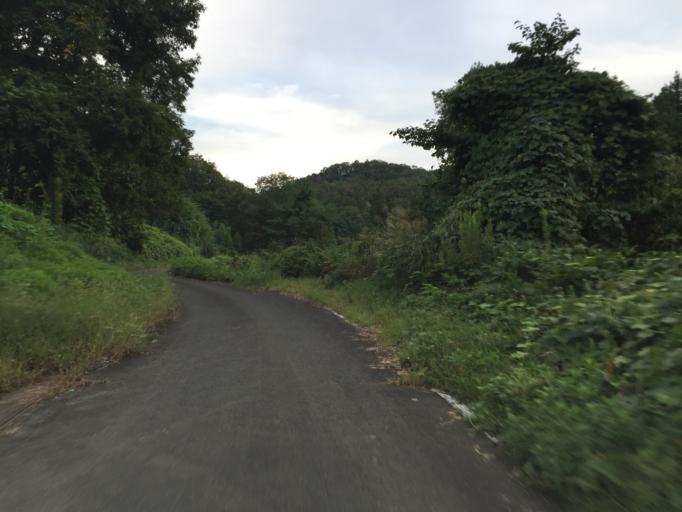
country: JP
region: Fukushima
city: Fukushima-shi
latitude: 37.7616
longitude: 140.5014
